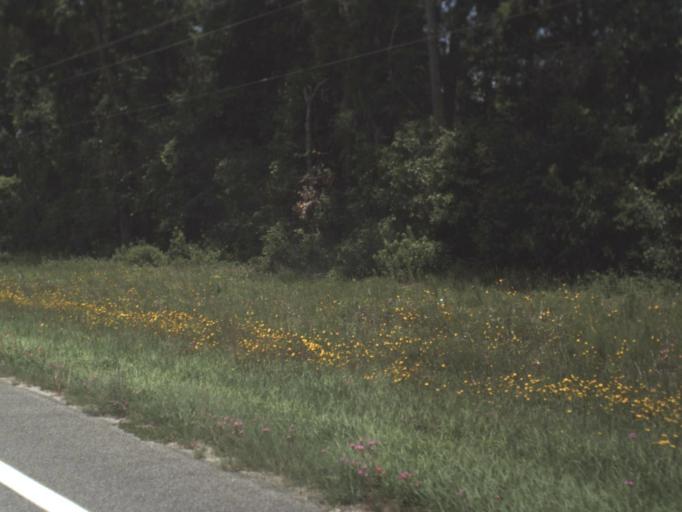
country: US
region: Florida
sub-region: Alachua County
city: High Springs
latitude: 29.9496
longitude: -82.7583
